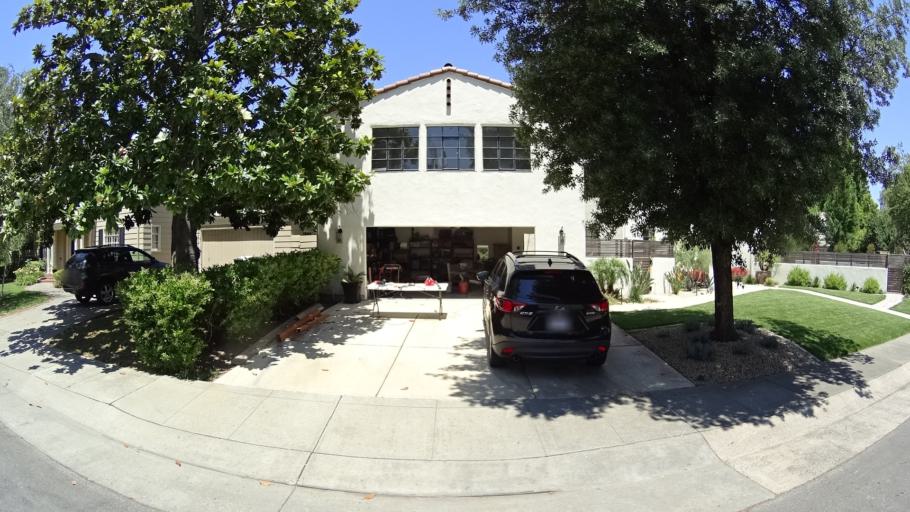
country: US
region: California
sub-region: Sacramento County
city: Sacramento
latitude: 38.5556
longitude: -121.5015
